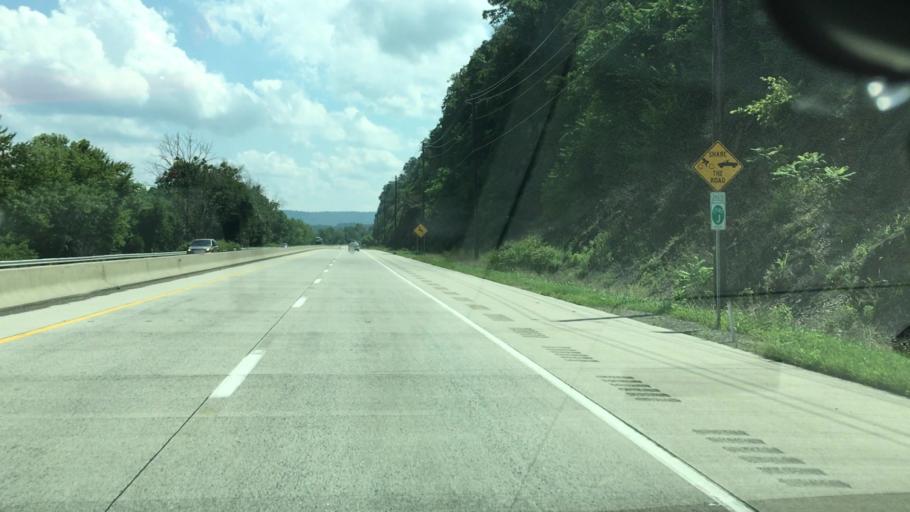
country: US
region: Pennsylvania
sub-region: Dauphin County
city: Matamoras
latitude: 40.4800
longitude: -76.9493
